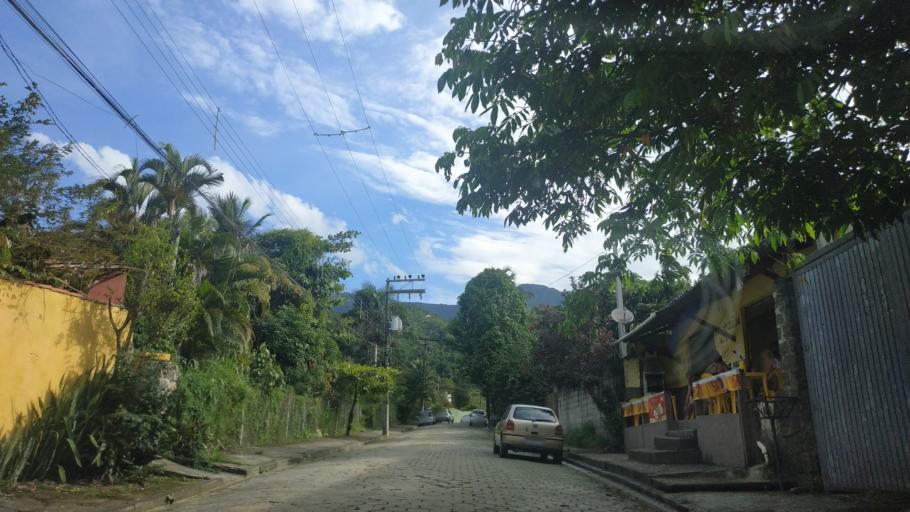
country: BR
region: Sao Paulo
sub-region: Ilhabela
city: Ilhabela
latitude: -23.8286
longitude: -45.3607
